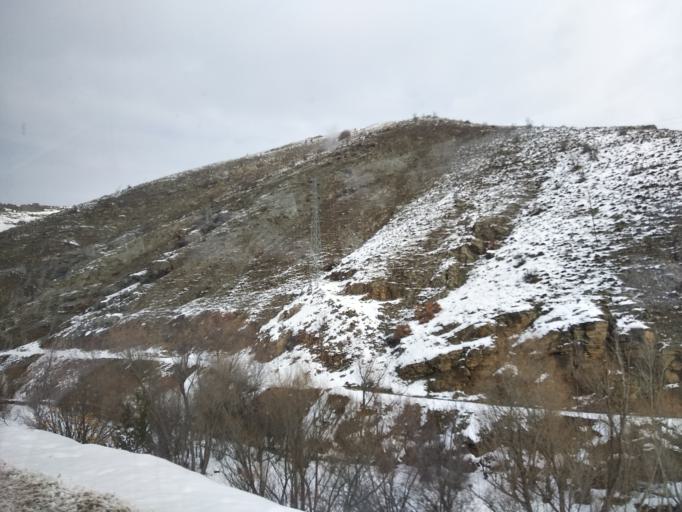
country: TR
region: Gumushane
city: Gumushkhane
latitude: 40.2902
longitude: 39.4831
